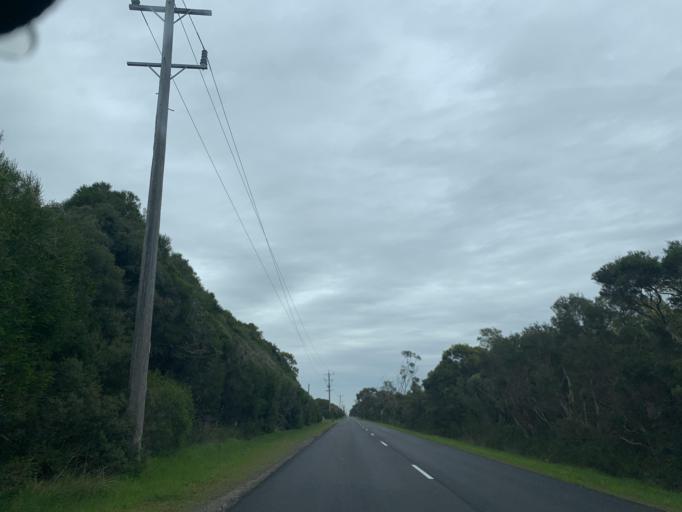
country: AU
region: Victoria
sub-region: Cardinia
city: Garfield
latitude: -38.0847
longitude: 145.6189
